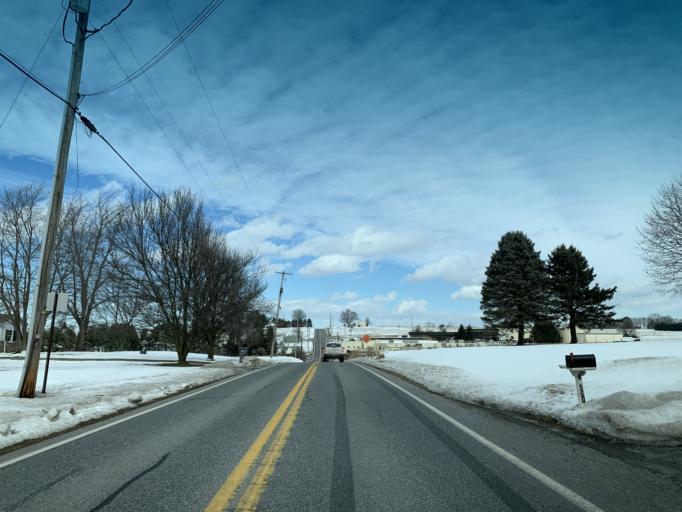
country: US
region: Pennsylvania
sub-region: York County
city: Dallastown
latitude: 39.8271
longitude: -76.6257
